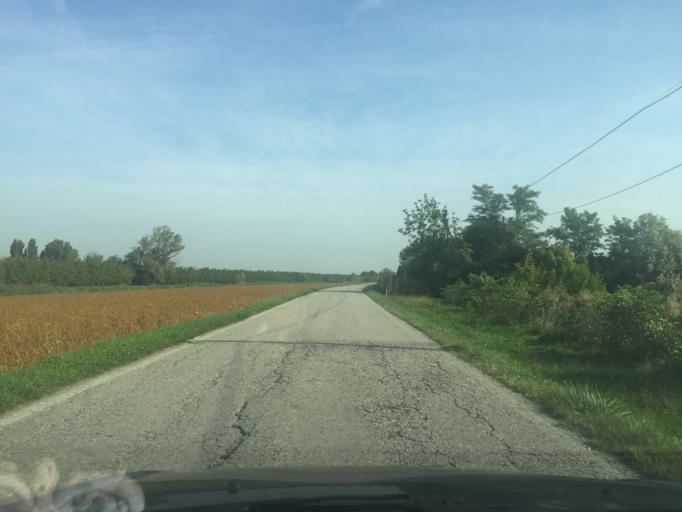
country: IT
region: Veneto
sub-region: Provincia di Venezia
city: Passarella
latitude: 45.6294
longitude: 12.6494
